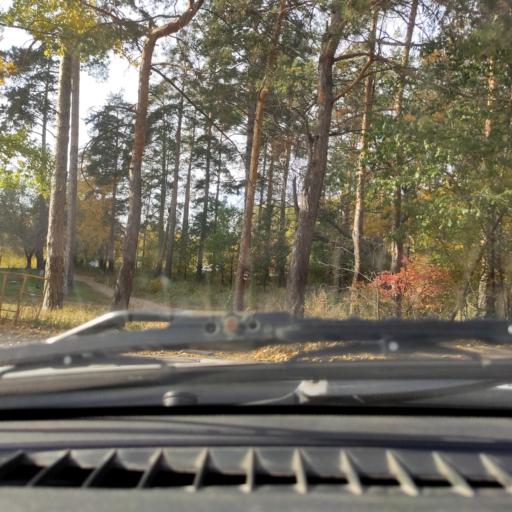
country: RU
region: Samara
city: Zhigulevsk
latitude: 53.4850
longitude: 49.4621
